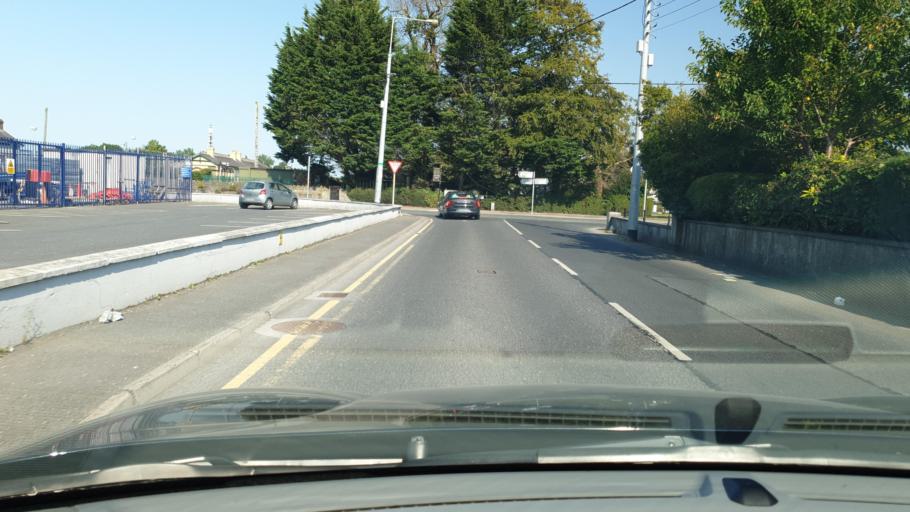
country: IE
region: Leinster
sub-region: An Mhi
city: Navan
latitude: 53.6480
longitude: -6.6866
